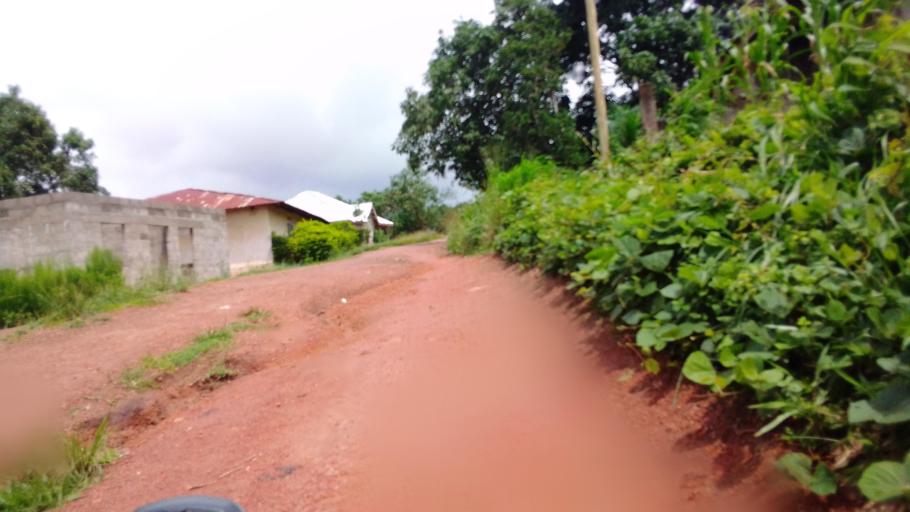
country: SL
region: Eastern Province
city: Kenema
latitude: 7.8634
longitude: -11.1737
